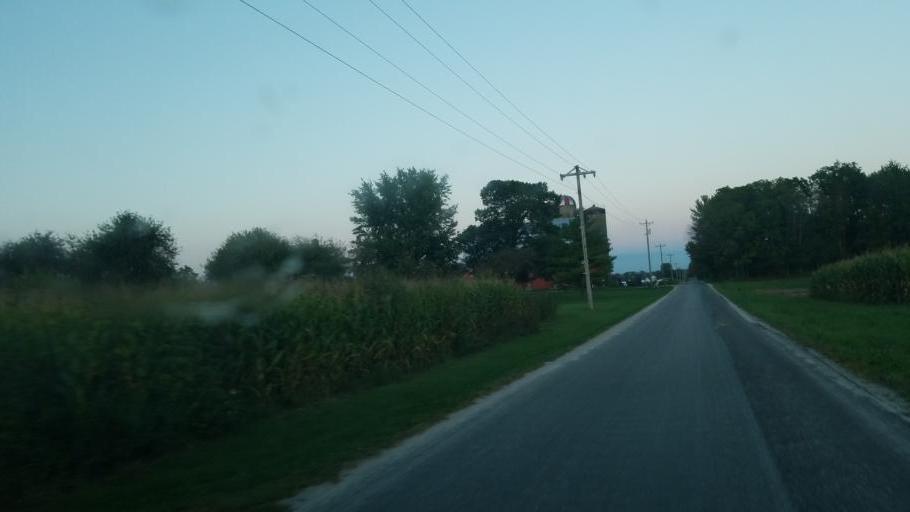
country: US
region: Ohio
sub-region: Ashland County
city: Ashland
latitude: 40.9313
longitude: -82.4061
